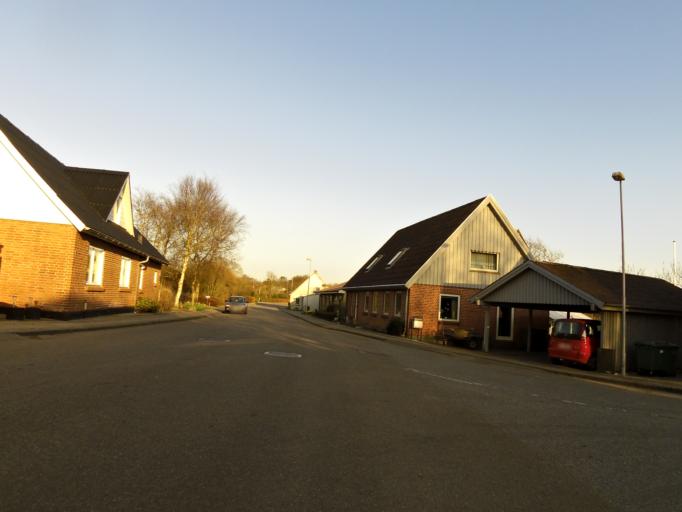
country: DK
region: Central Jutland
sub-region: Holstebro Kommune
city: Vinderup
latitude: 56.5216
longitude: 8.7845
